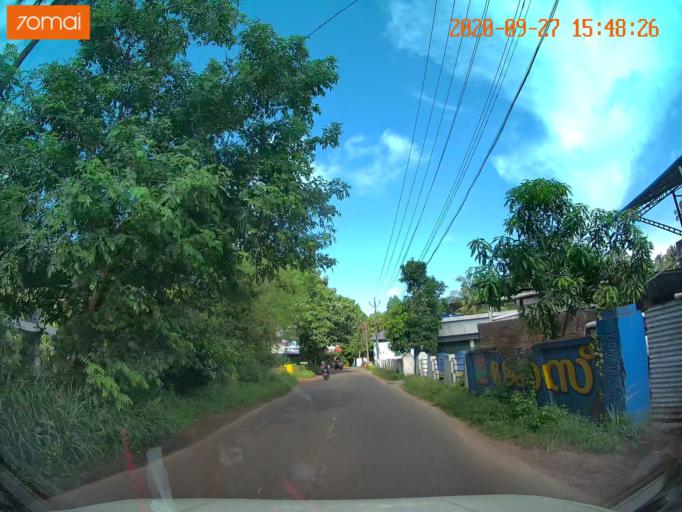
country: IN
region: Kerala
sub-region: Thrissur District
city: Thanniyam
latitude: 10.4832
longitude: 76.1343
